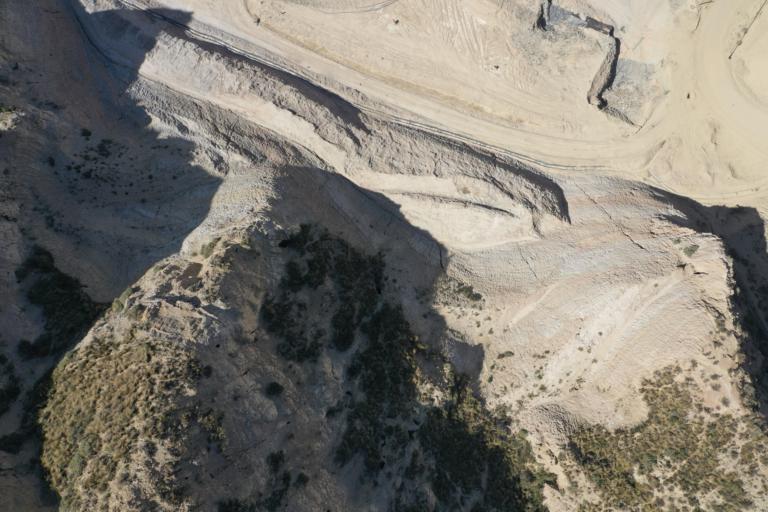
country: BO
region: La Paz
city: La Paz
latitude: -16.5537
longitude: -68.1255
